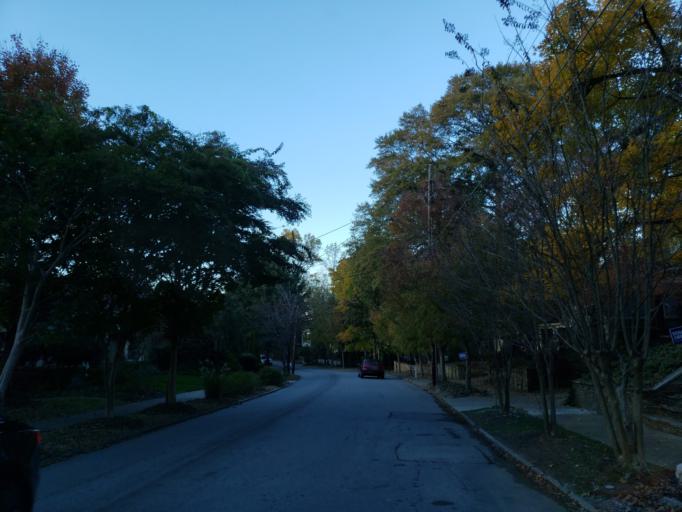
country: US
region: Georgia
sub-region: DeKalb County
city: Druid Hills
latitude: 33.7832
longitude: -84.3637
